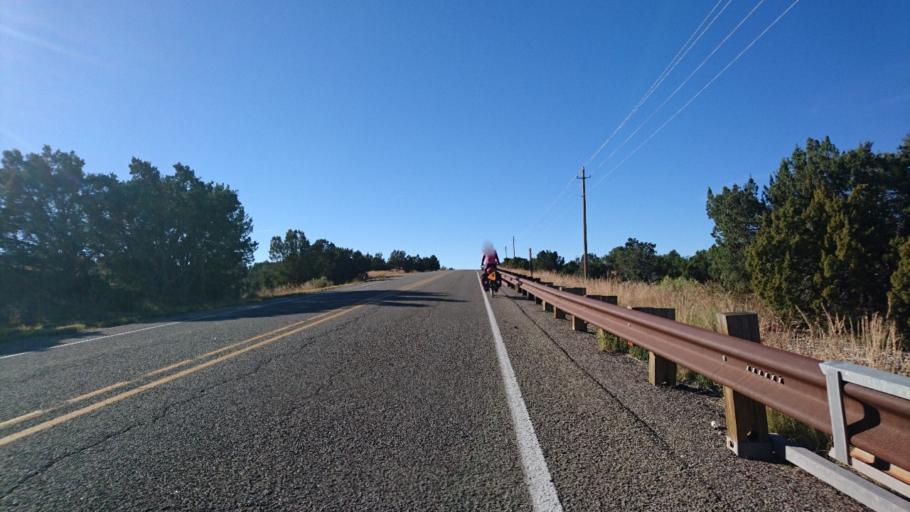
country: US
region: New Mexico
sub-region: Santa Fe County
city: La Cienega
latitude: 35.4734
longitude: -106.0693
